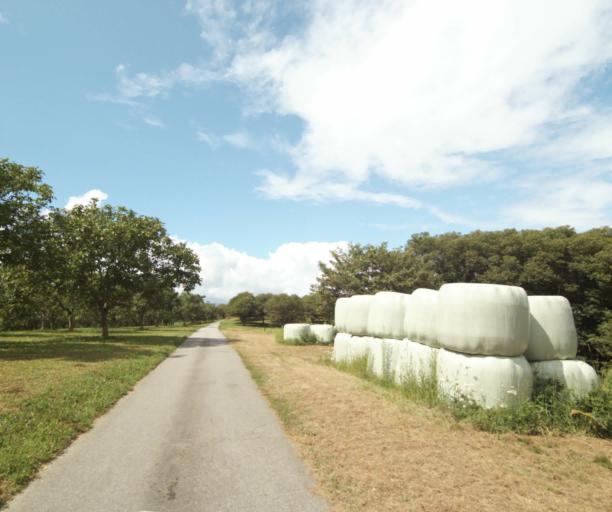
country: FR
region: Limousin
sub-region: Departement de la Correze
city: Sainte-Fortunade
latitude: 45.1720
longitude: 1.8379
